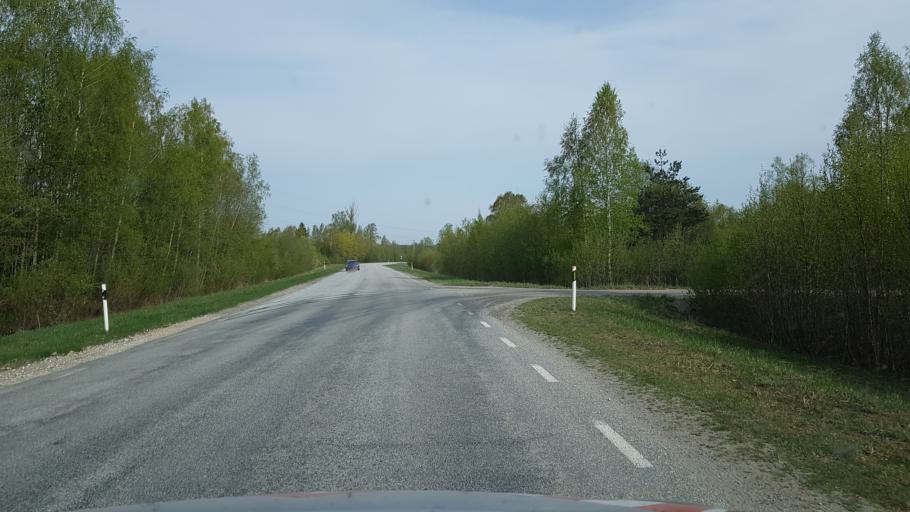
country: EE
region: Paernumaa
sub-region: Audru vald
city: Audru
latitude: 58.4190
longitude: 24.3108
